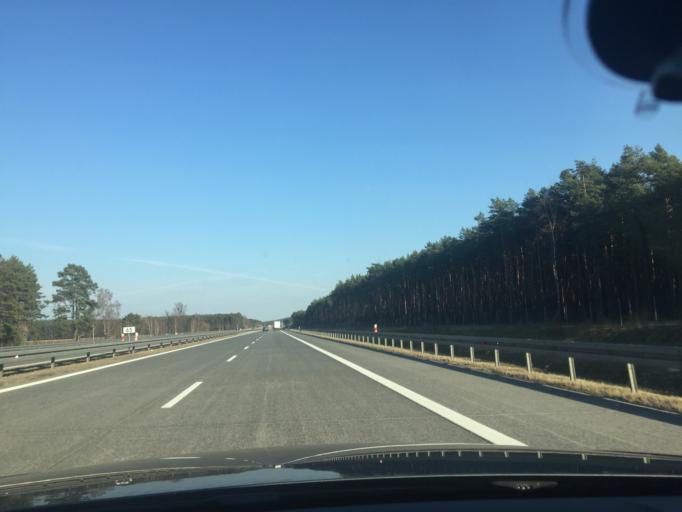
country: PL
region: Lubusz
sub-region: Powiat swiebodzinski
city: Lubrza
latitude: 52.3196
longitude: 15.4978
